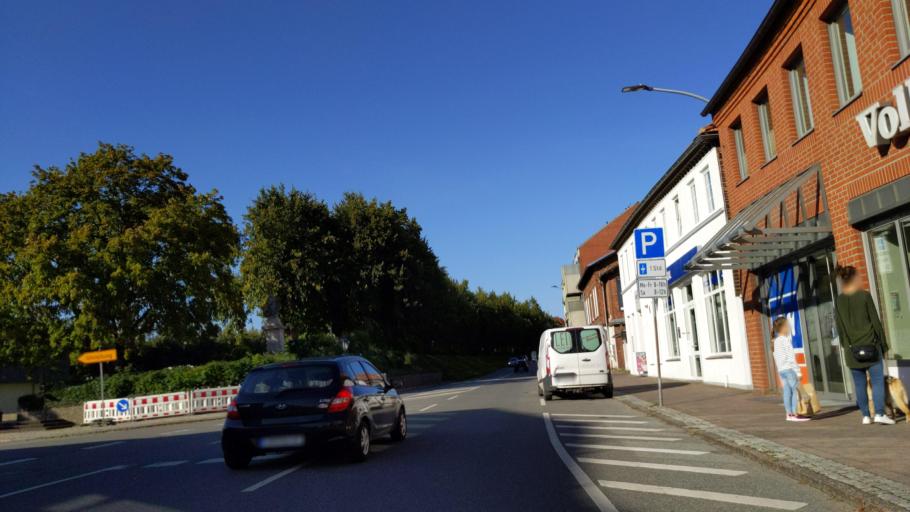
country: DE
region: Schleswig-Holstein
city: Ahrensbok
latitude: 54.0107
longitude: 10.5732
